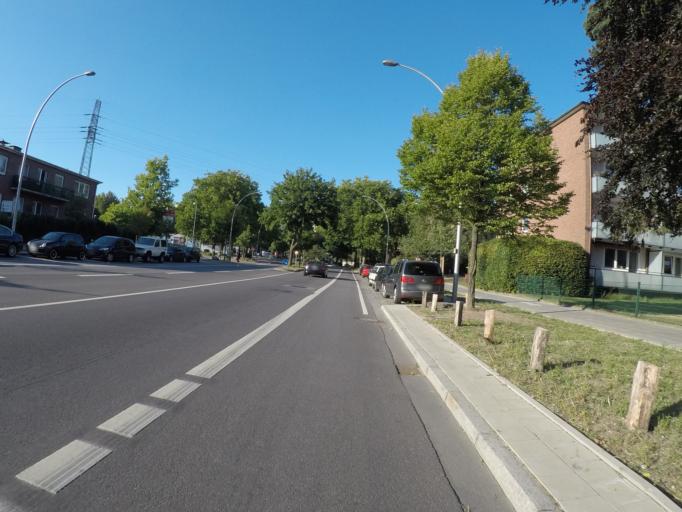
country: DE
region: Hamburg
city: Steilshoop
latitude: 53.6068
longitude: 10.0564
